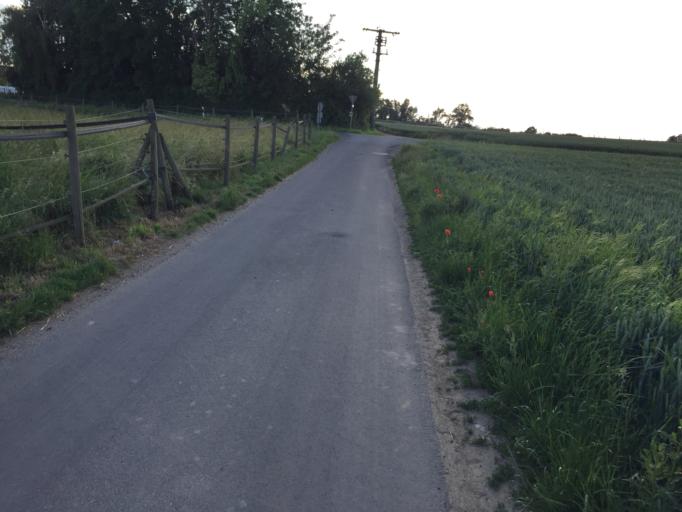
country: DE
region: Hesse
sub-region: Regierungsbezirk Darmstadt
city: Niederdorfelden
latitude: 50.2092
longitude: 8.7890
